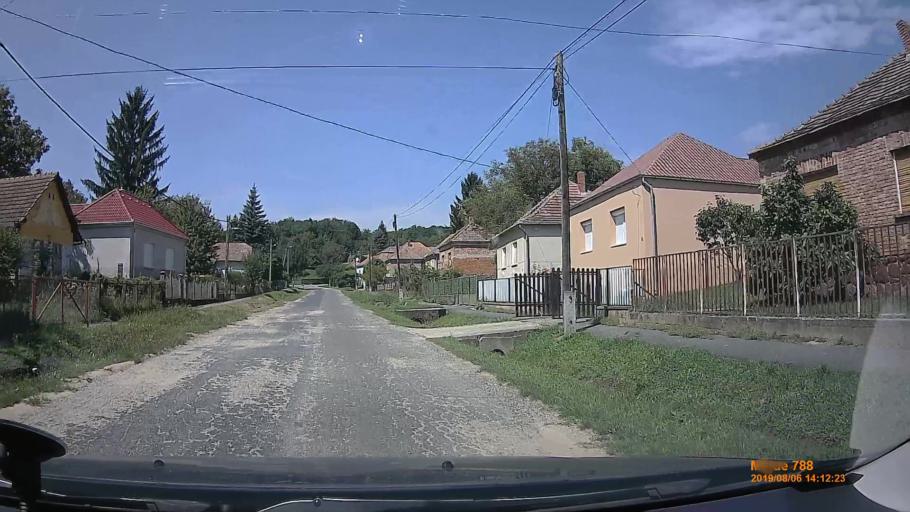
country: HU
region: Zala
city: Zalakomar
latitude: 46.5615
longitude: 17.0778
